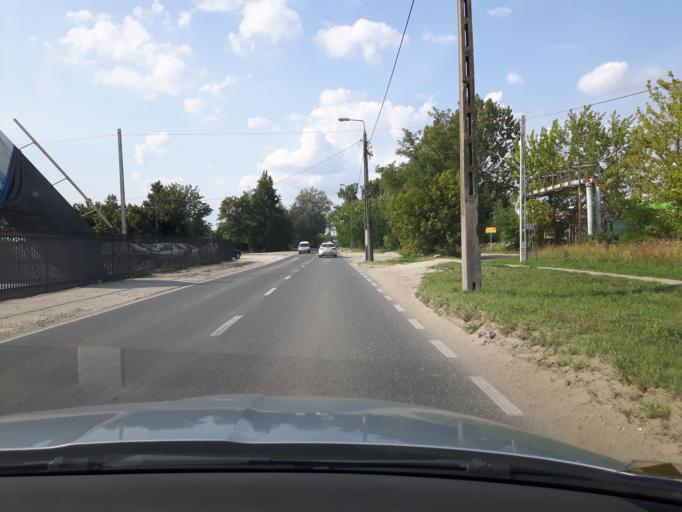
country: PL
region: Masovian Voivodeship
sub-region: Powiat wolominski
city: Zabki
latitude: 52.2718
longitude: 21.1186
